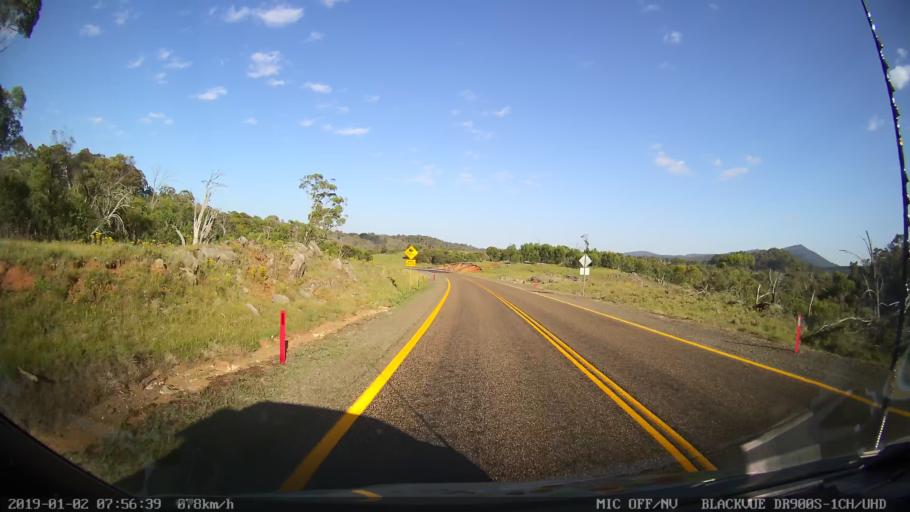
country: AU
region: New South Wales
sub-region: Tumut Shire
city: Tumut
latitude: -35.6687
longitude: 148.4833
